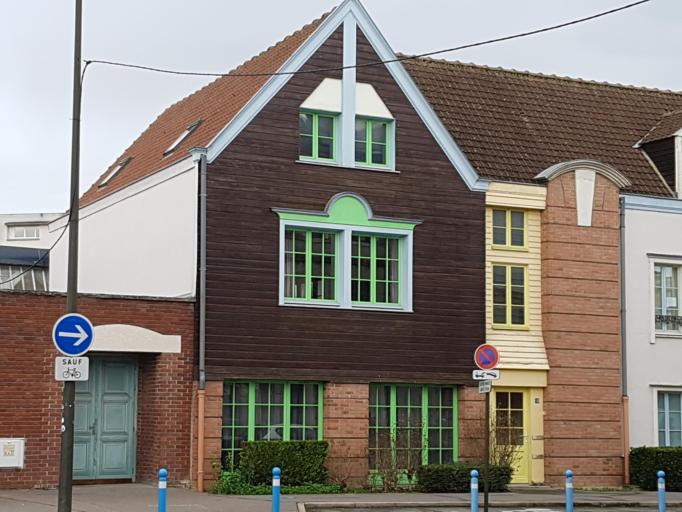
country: FR
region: Picardie
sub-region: Departement de la Somme
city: Amiens
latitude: 49.9003
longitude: 2.3006
